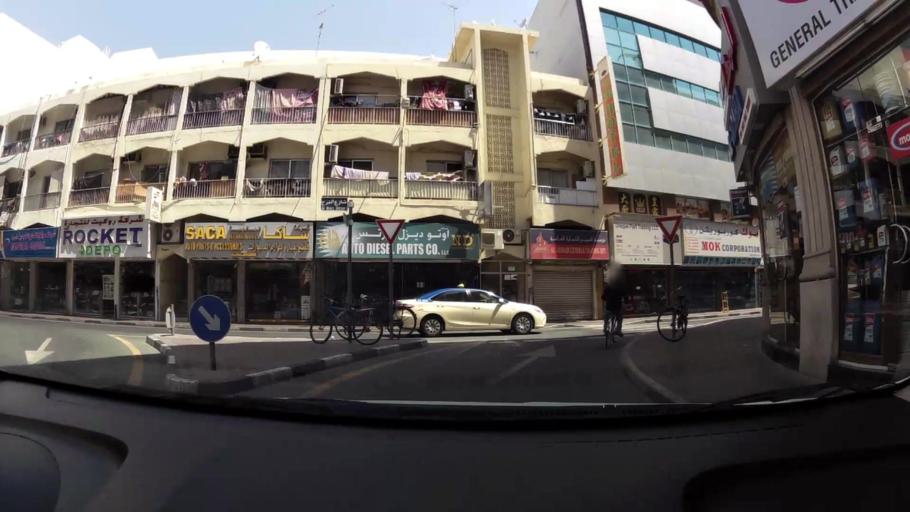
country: AE
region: Ash Shariqah
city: Sharjah
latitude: 25.2698
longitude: 55.3091
